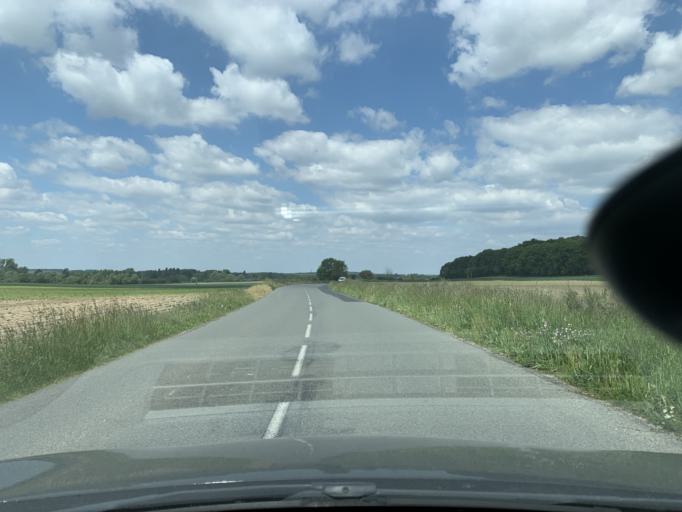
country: FR
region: Nord-Pas-de-Calais
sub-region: Departement du Pas-de-Calais
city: Oisy-le-Verger
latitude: 50.2554
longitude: 3.1123
